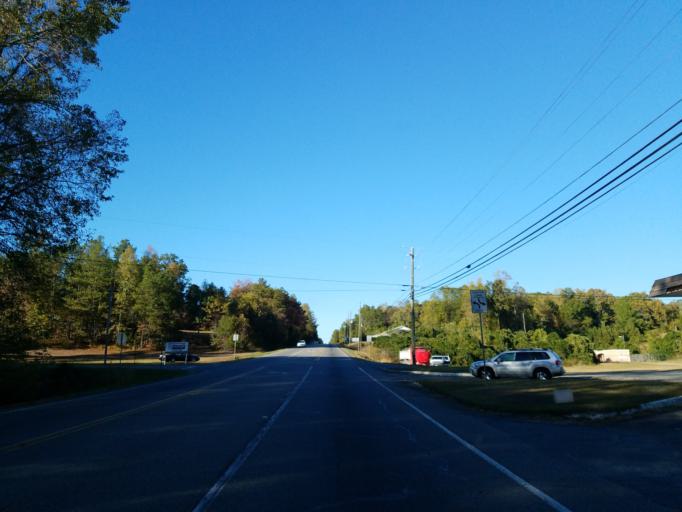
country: US
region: Georgia
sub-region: Cherokee County
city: Ball Ground
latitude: 34.3476
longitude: -84.3800
